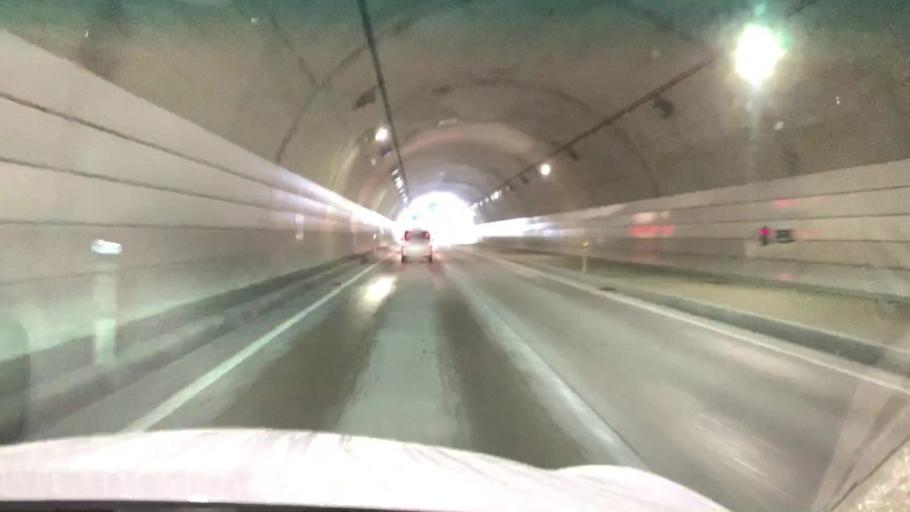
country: JP
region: Toyama
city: Kamiichi
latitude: 36.5751
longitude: 137.3534
